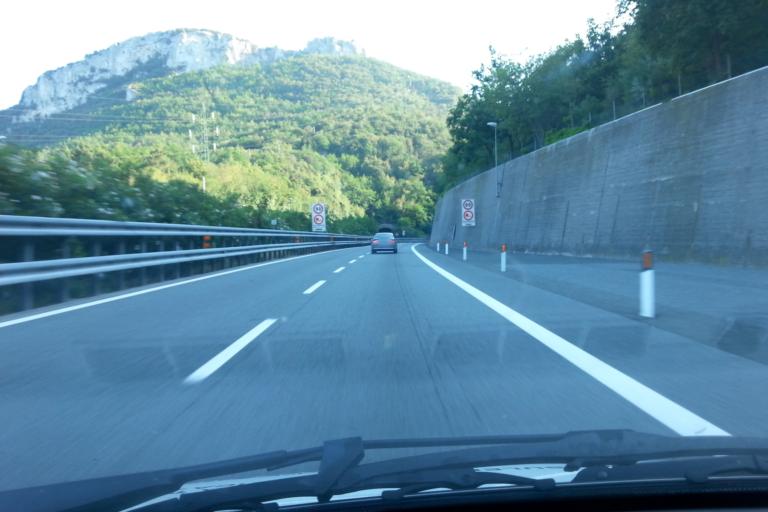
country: IT
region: Liguria
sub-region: Provincia di Savona
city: Feglino
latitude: 44.2125
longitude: 8.3210
